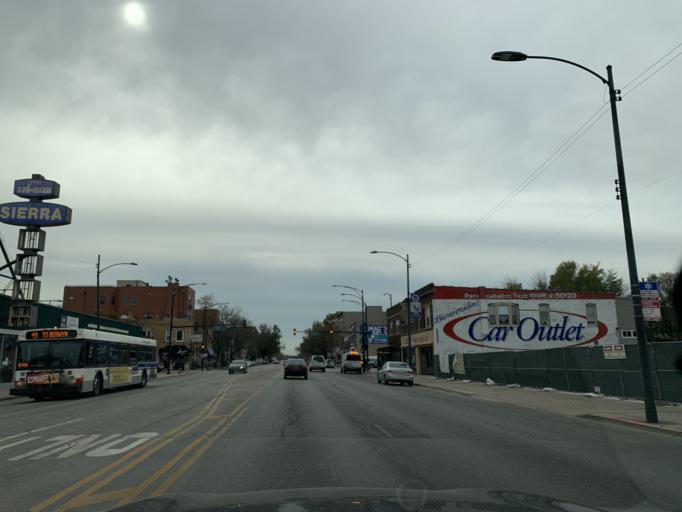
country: US
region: Illinois
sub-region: Cook County
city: Lincolnwood
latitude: 41.9584
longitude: -87.6886
